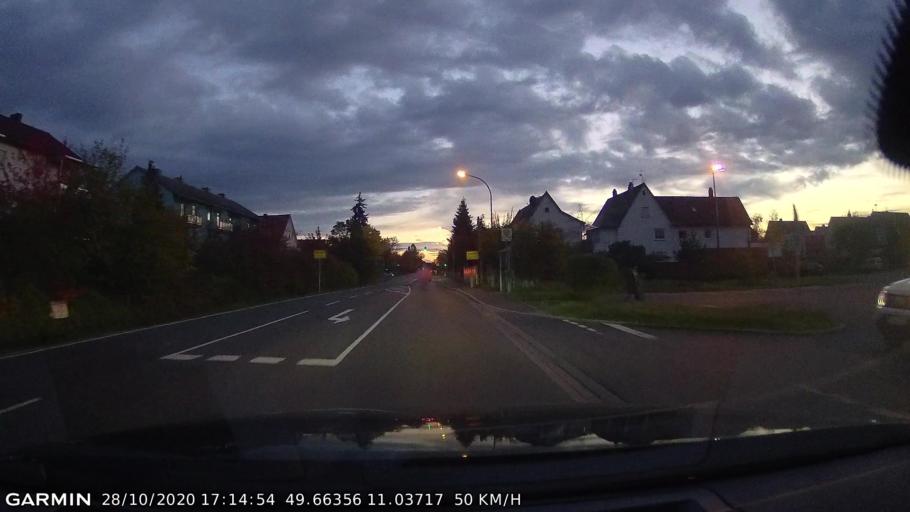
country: DE
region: Bavaria
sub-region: Regierungsbezirk Mittelfranken
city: Baiersdorf
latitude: 49.6634
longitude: 11.0370
